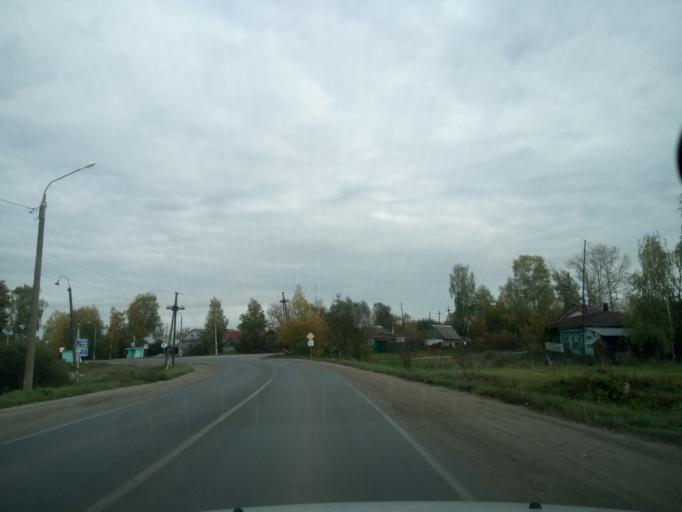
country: RU
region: Nizjnij Novgorod
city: Lukoyanov
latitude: 55.0294
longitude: 44.4676
